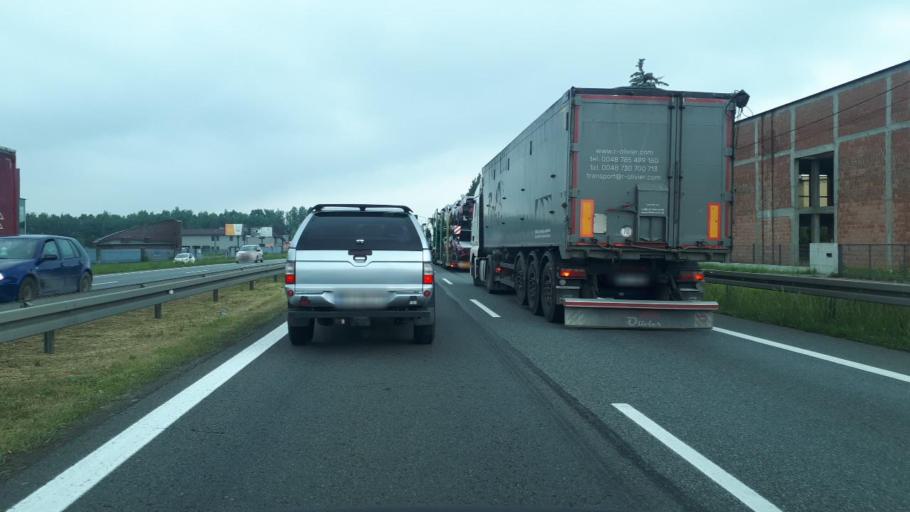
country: PL
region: Silesian Voivodeship
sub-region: Powiat pszczynski
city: Goczalkowice Zdroj
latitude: 49.9617
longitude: 18.9607
